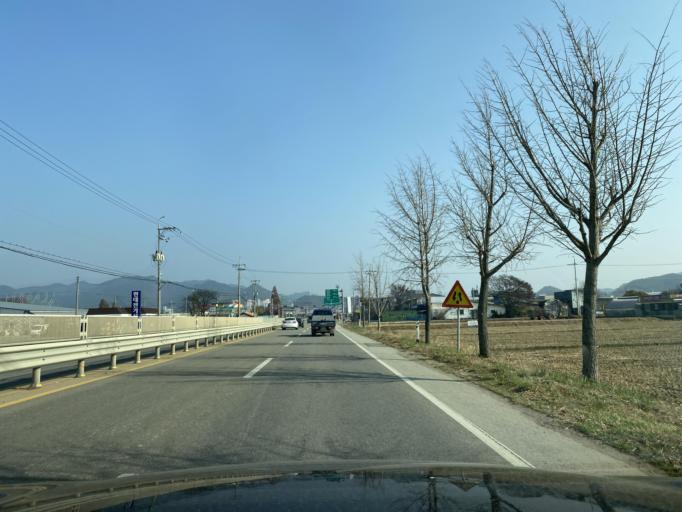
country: KR
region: Chungcheongnam-do
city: Yesan
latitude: 36.6849
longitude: 126.8134
